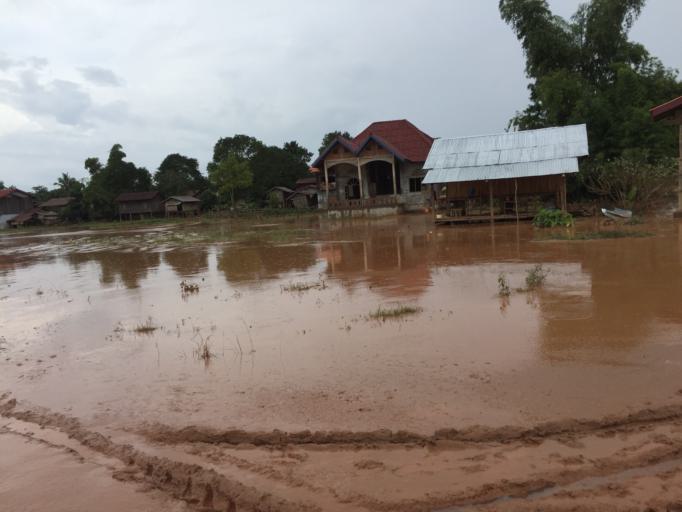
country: LA
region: Attapu
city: Attapu
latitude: 14.6980
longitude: 106.5318
